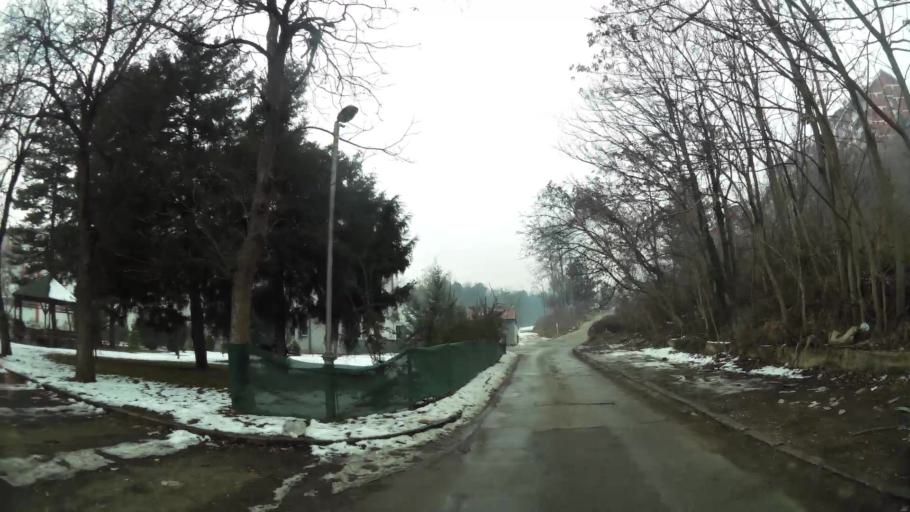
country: MK
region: Cair
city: Cair
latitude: 42.0086
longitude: 21.4604
